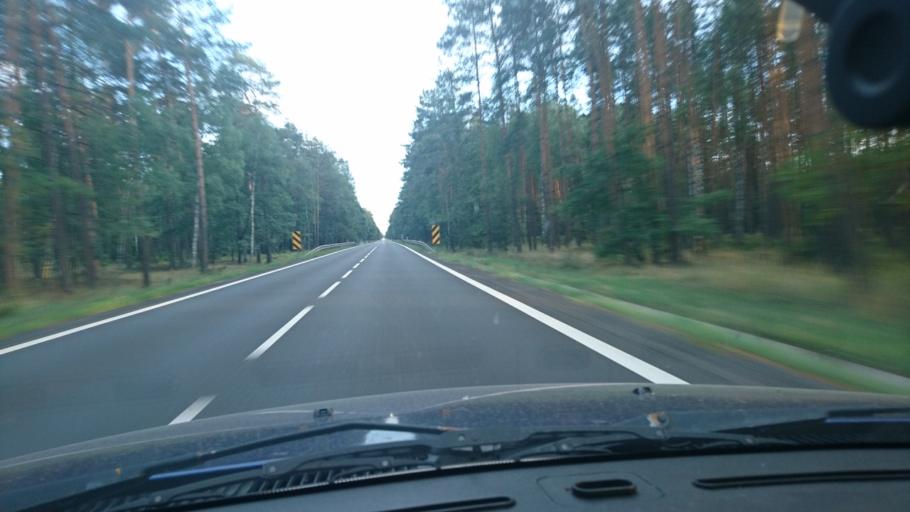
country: PL
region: Silesian Voivodeship
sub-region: Powiat tarnogorski
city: Tworog
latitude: 50.5799
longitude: 18.7082
